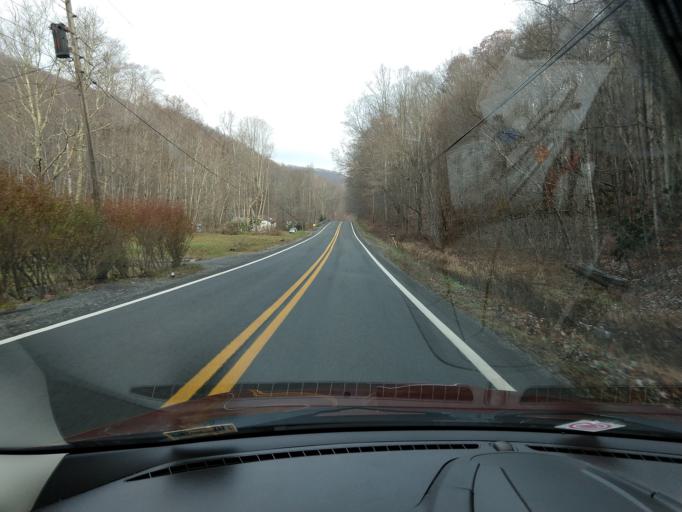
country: US
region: West Virginia
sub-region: Greenbrier County
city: Rainelle
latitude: 38.0742
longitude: -80.7070
